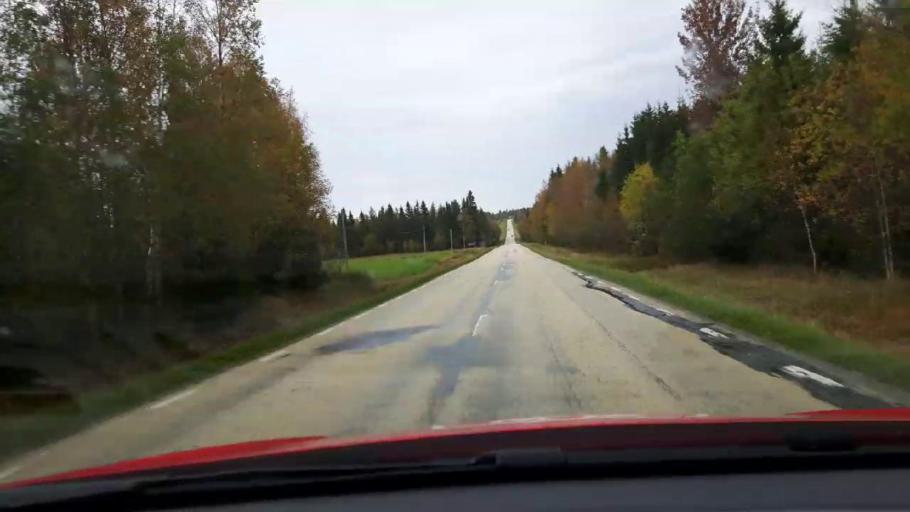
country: SE
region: Jaemtland
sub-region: Bergs Kommun
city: Hoverberg
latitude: 62.9272
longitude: 14.3353
